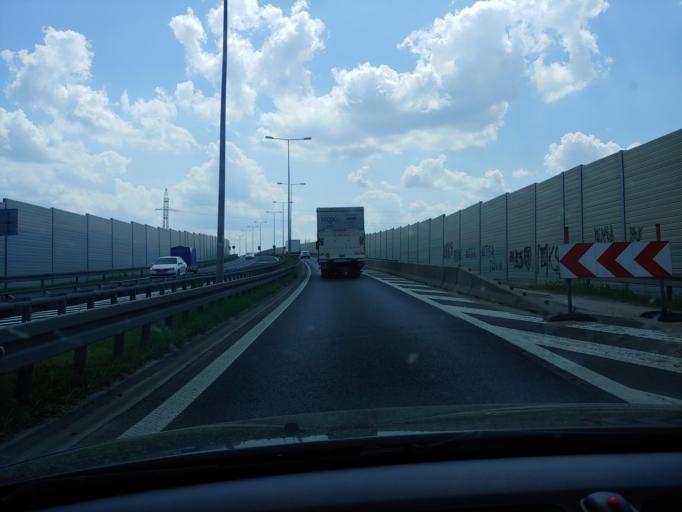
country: PL
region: Lesser Poland Voivodeship
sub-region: Powiat tarnowski
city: Lisia Gora
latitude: 50.0569
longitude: 21.0107
